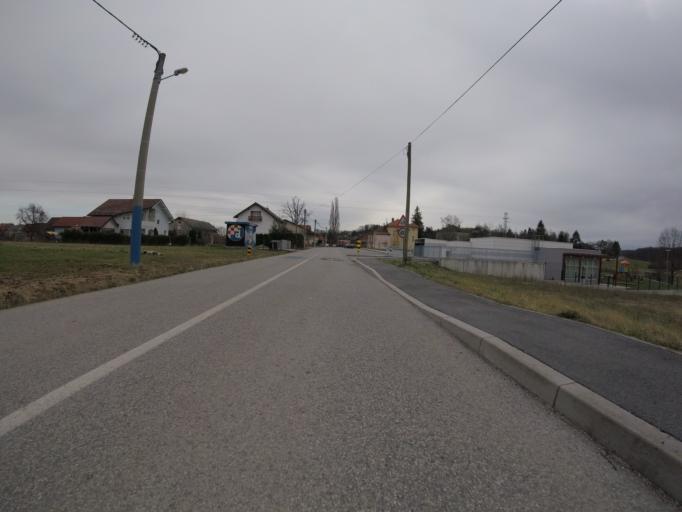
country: HR
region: Grad Zagreb
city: Strmec
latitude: 45.6637
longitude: 15.9412
